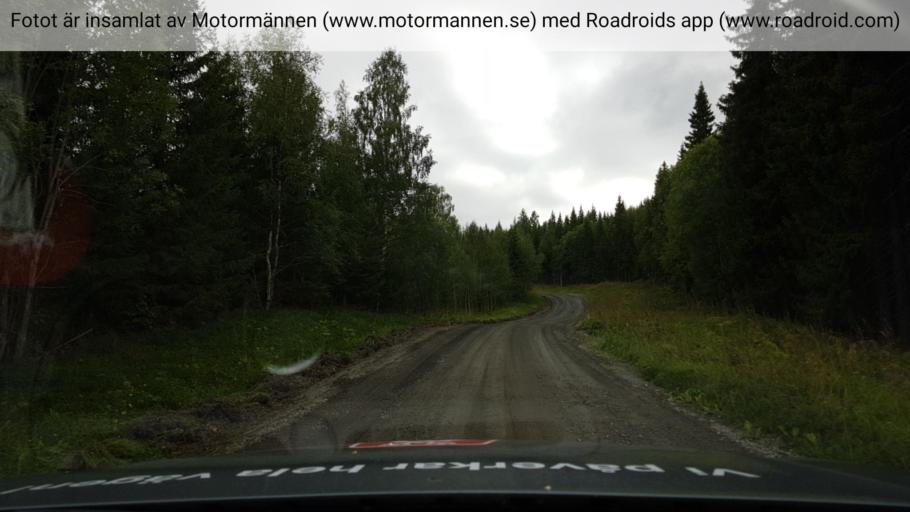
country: SE
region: Jaemtland
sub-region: Krokoms Kommun
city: Valla
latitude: 63.3953
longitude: 14.0656
